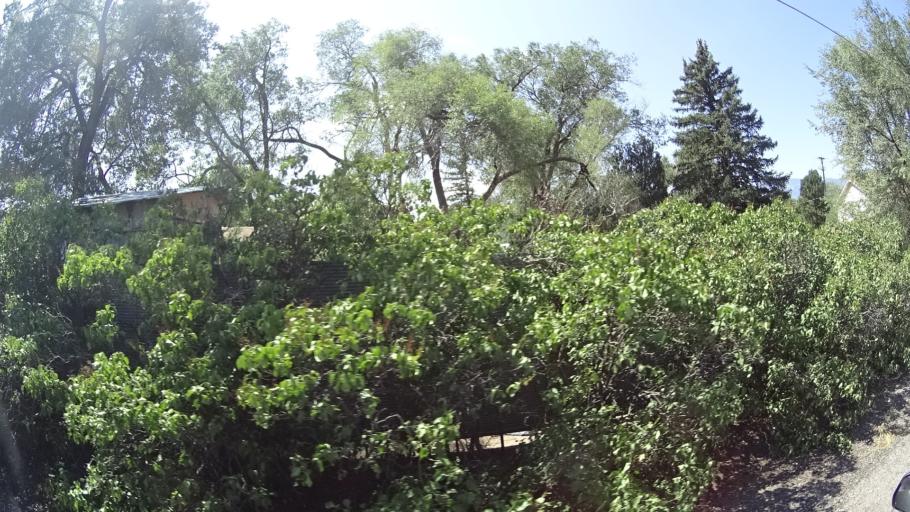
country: US
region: Colorado
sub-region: El Paso County
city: Colorado Springs
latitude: 38.8704
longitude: -104.8168
